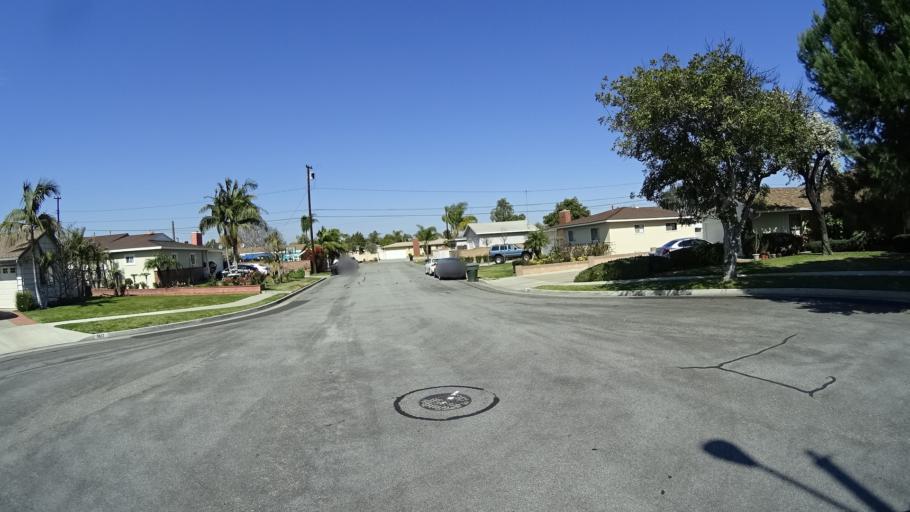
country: US
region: California
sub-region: Orange County
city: Garden Grove
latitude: 33.8076
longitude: -117.9521
